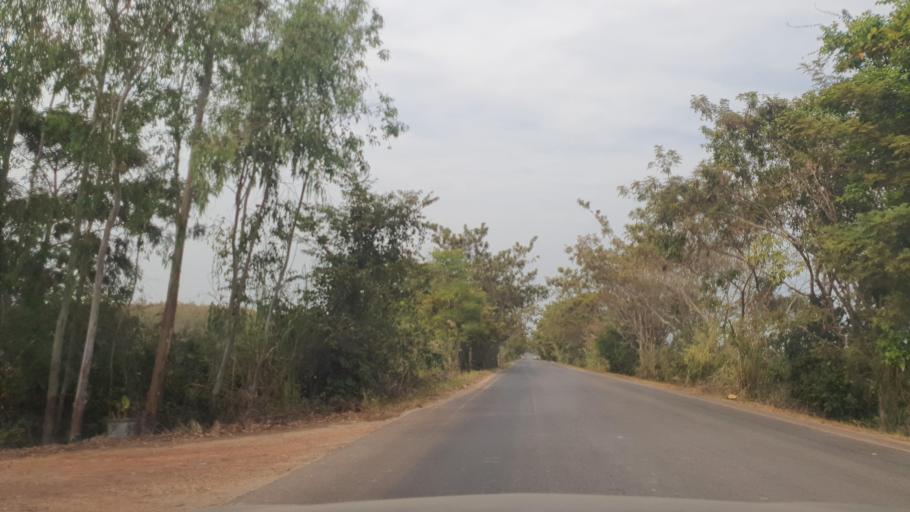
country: TH
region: Changwat Bueng Kan
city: Bung Khla
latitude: 18.2200
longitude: 104.0382
